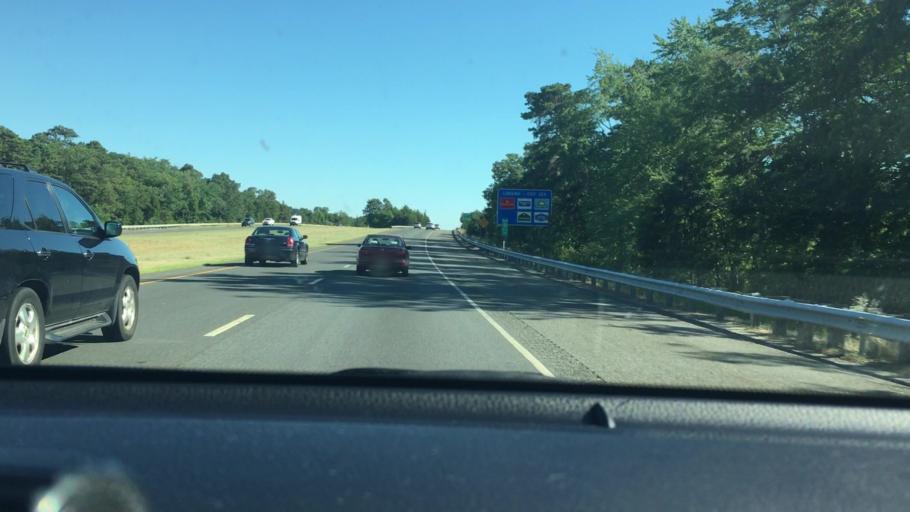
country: US
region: New Jersey
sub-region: Cumberland County
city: Vineland
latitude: 39.5081
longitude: -75.0696
